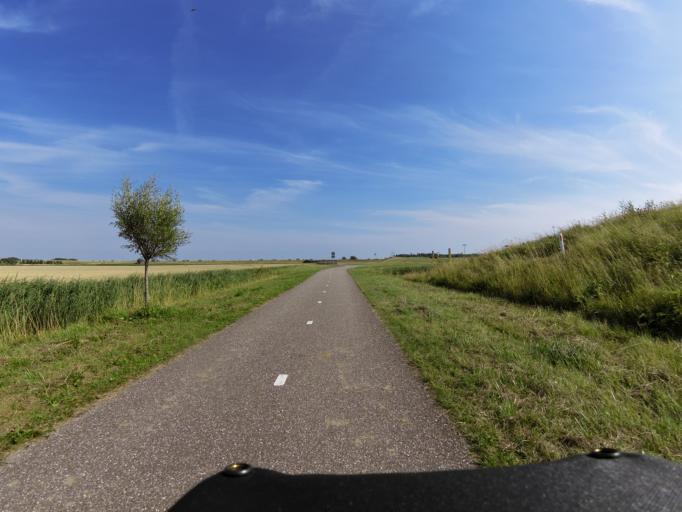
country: NL
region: South Holland
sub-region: Gemeente Goeree-Overflakkee
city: Ouddorp
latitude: 51.7960
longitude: 3.8807
